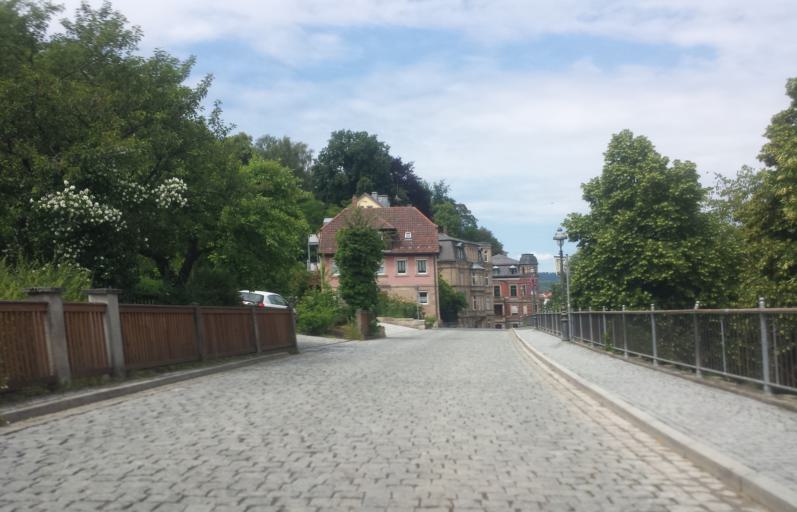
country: DE
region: Bavaria
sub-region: Upper Franconia
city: Kulmbach
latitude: 50.1056
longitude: 11.4579
